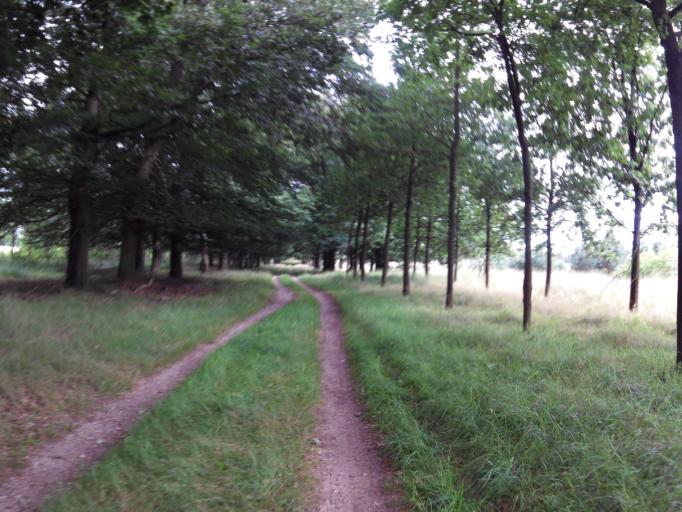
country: NL
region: Gelderland
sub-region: Gemeente Rozendaal
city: Rozendaal
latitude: 52.0496
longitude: 5.9201
